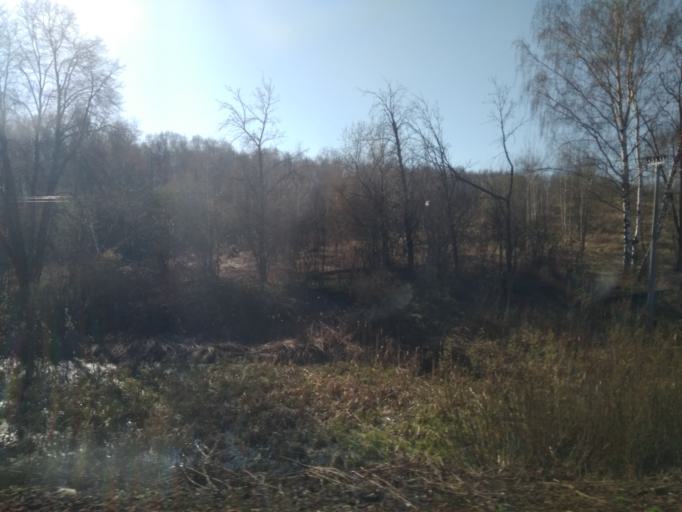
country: RU
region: Moskovskaya
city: Pavshino
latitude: 55.8231
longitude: 37.3610
